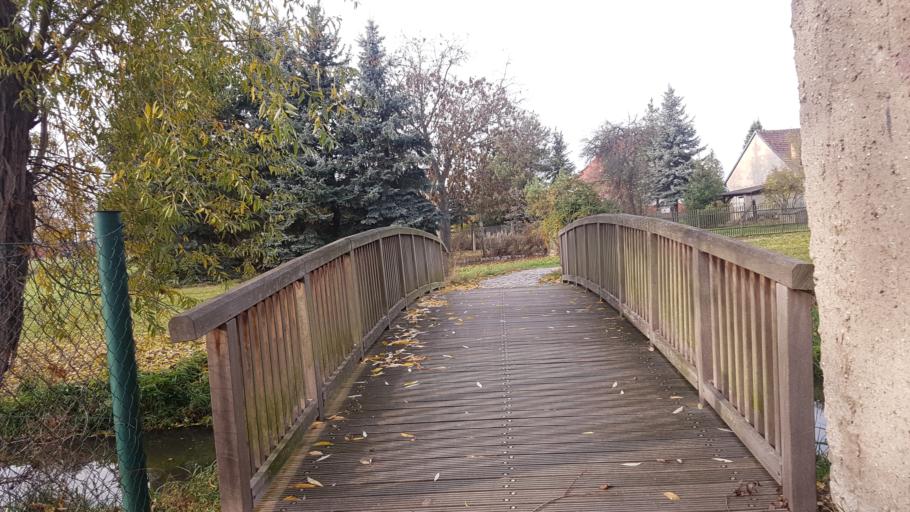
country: DE
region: Brandenburg
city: Falkenberg
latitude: 51.5955
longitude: 13.2962
